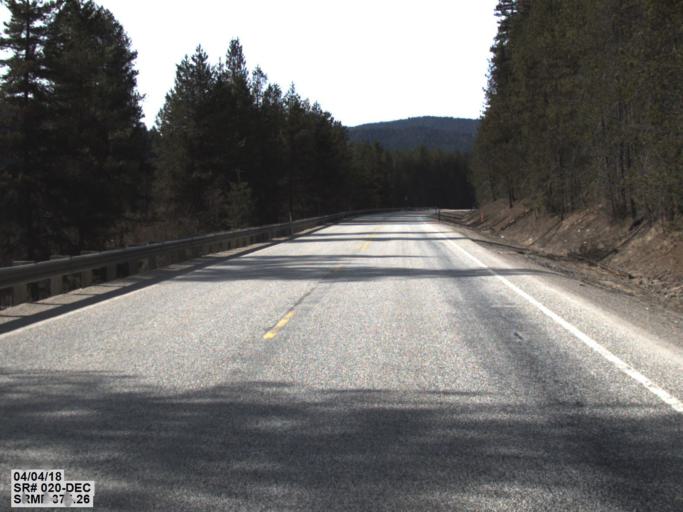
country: US
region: Washington
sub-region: Stevens County
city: Chewelah
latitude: 48.5591
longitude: -117.5572
